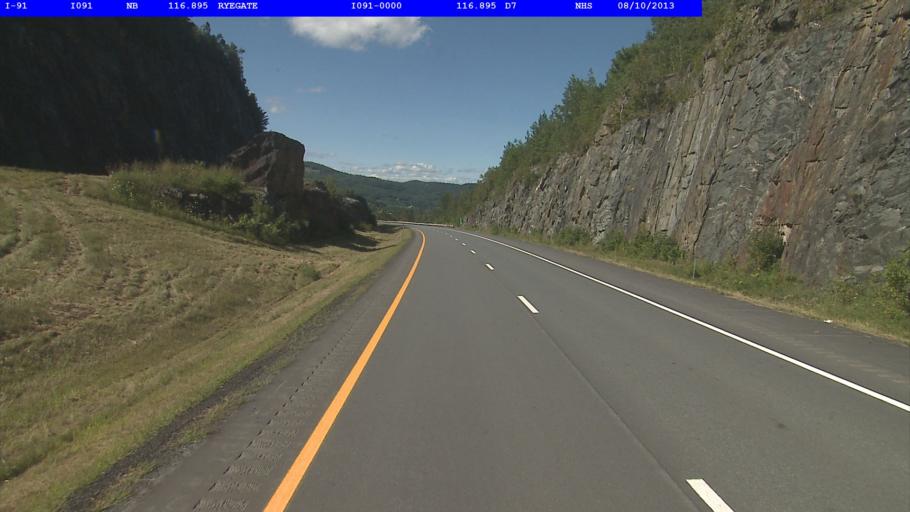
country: US
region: New Hampshire
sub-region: Grafton County
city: Woodsville
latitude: 44.2511
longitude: -72.0611
